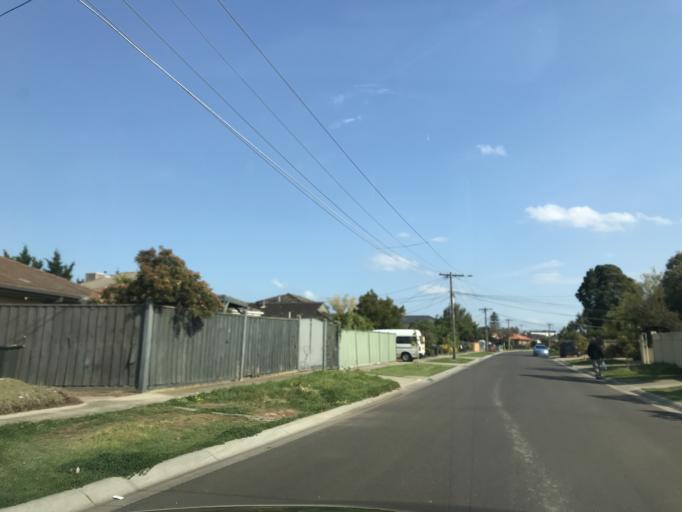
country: AU
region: Victoria
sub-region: Wyndham
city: Hoppers Crossing
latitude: -37.8762
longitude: 144.7008
